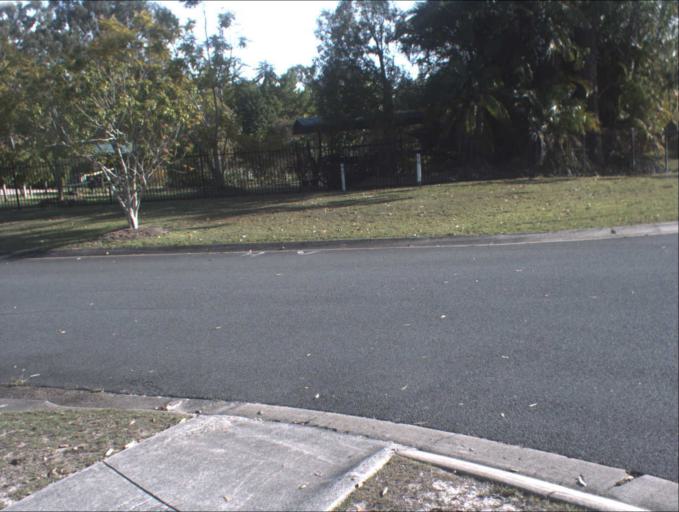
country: AU
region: Queensland
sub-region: Logan
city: Park Ridge South
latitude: -27.7030
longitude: 153.0256
